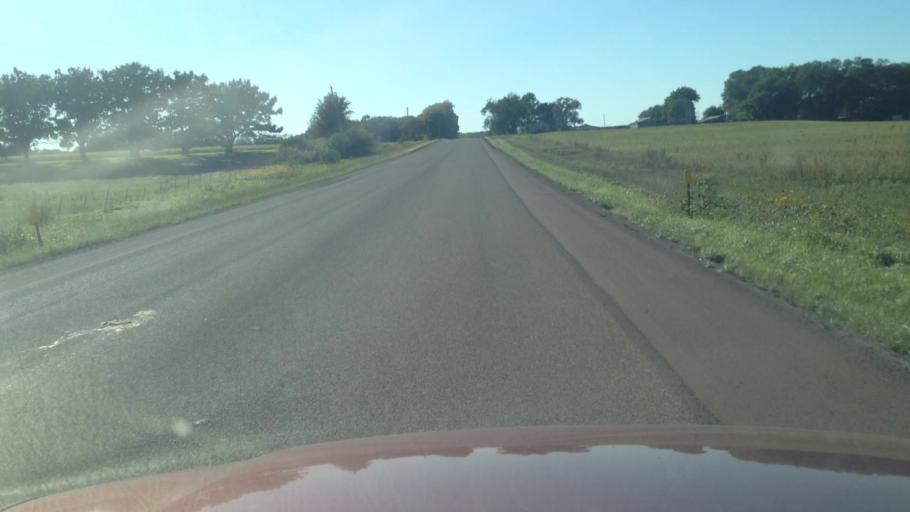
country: US
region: Kansas
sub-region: Douglas County
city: Eudora
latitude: 38.9425
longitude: -95.1534
